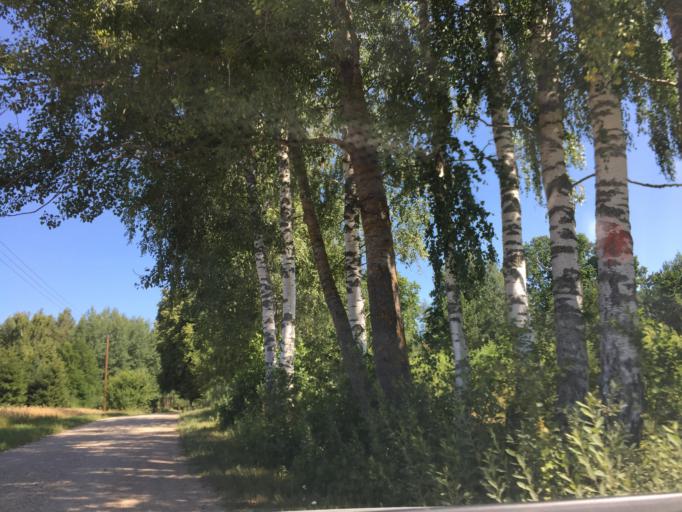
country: LV
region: Talsu Rajons
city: Stende
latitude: 57.1641
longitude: 22.2972
